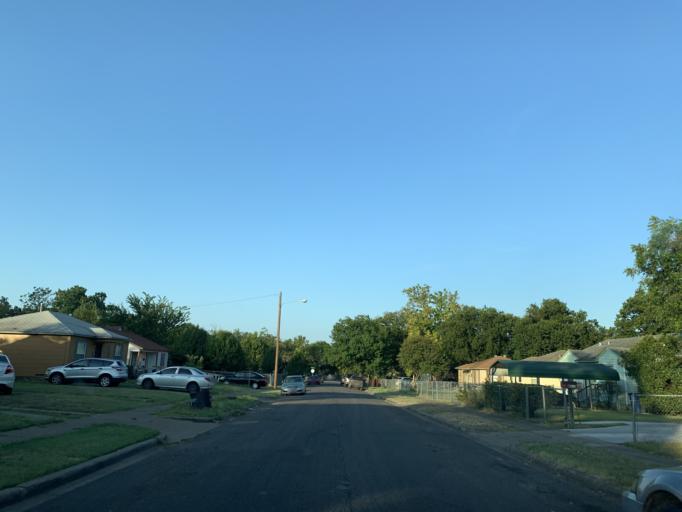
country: US
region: Texas
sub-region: Dallas County
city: Dallas
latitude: 32.7067
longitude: -96.7861
